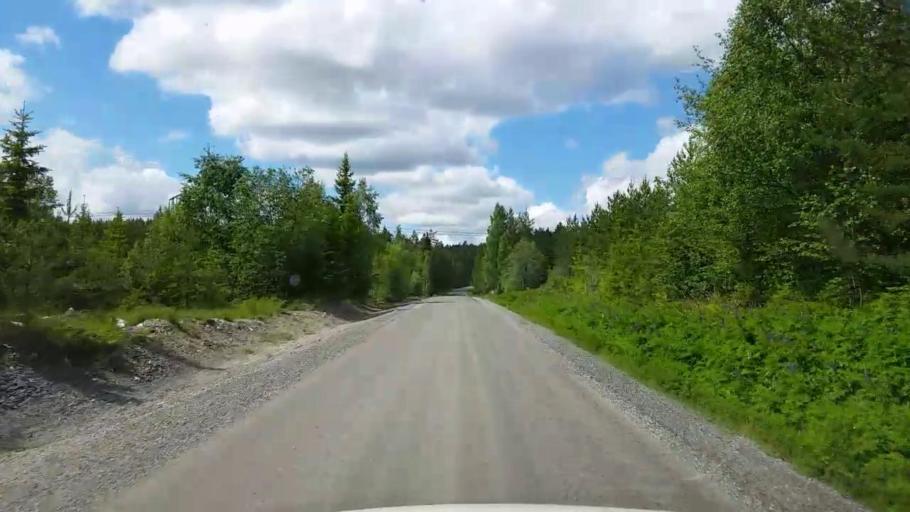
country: SE
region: Gaevleborg
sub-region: Bollnas Kommun
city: Vittsjo
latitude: 61.0909
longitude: 16.1791
